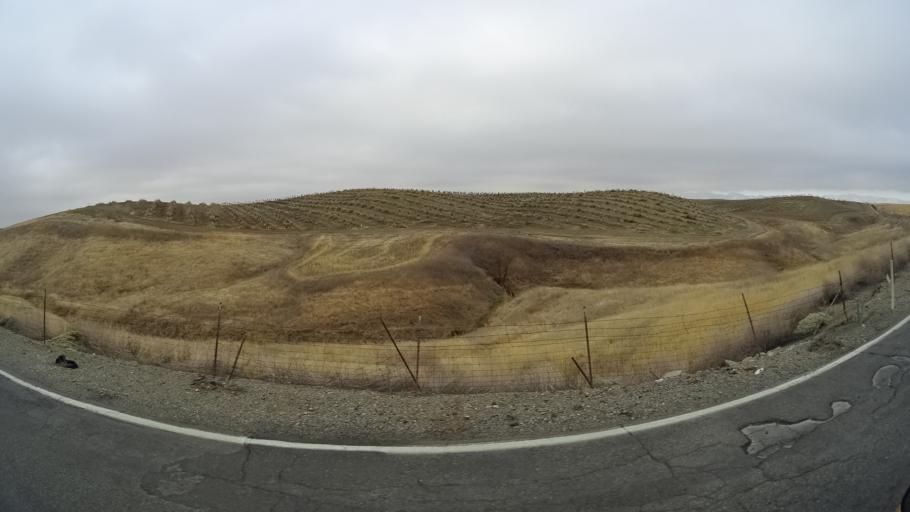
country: US
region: California
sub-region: Yolo County
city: Dunnigan
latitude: 38.8865
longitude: -122.0154
